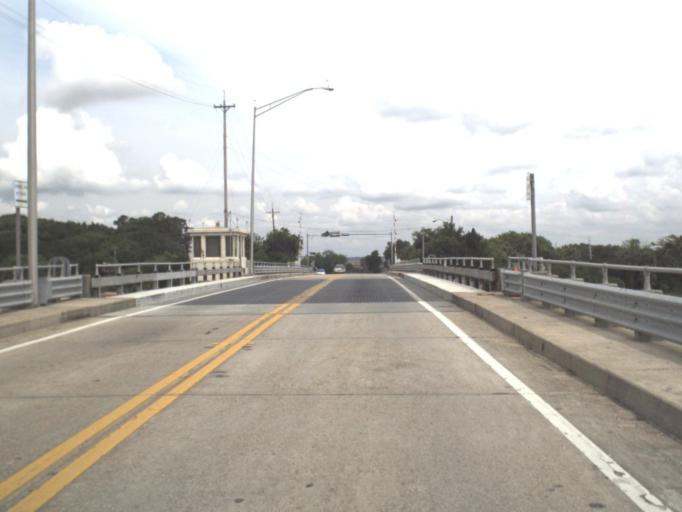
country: US
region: Florida
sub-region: Duval County
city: Atlantic Beach
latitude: 30.3937
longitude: -81.4596
